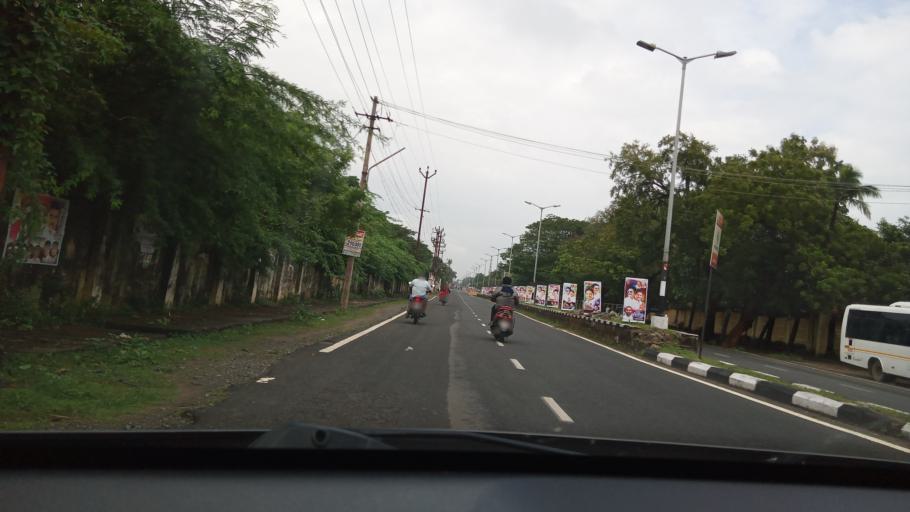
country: IN
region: Tamil Nadu
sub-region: Villupuram
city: Auroville
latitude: 12.0096
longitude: 79.8564
